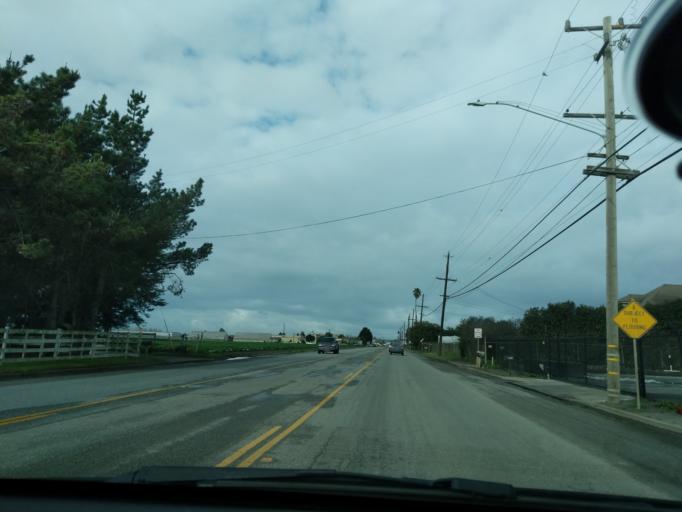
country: US
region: California
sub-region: Monterey County
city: Pajaro
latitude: 36.9044
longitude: -121.7380
